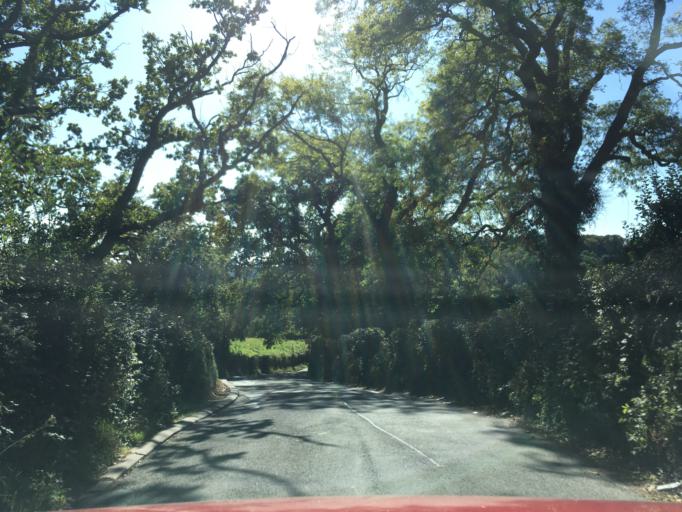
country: GB
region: Wales
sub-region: Torfaen County Borough
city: Ponthir
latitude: 51.6112
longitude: -2.9887
